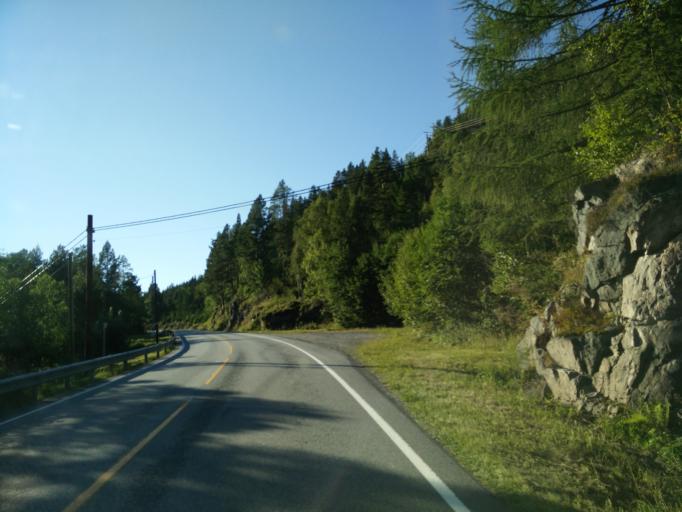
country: NO
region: More og Romsdal
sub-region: Halsa
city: Liaboen
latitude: 63.0239
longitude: 8.4731
